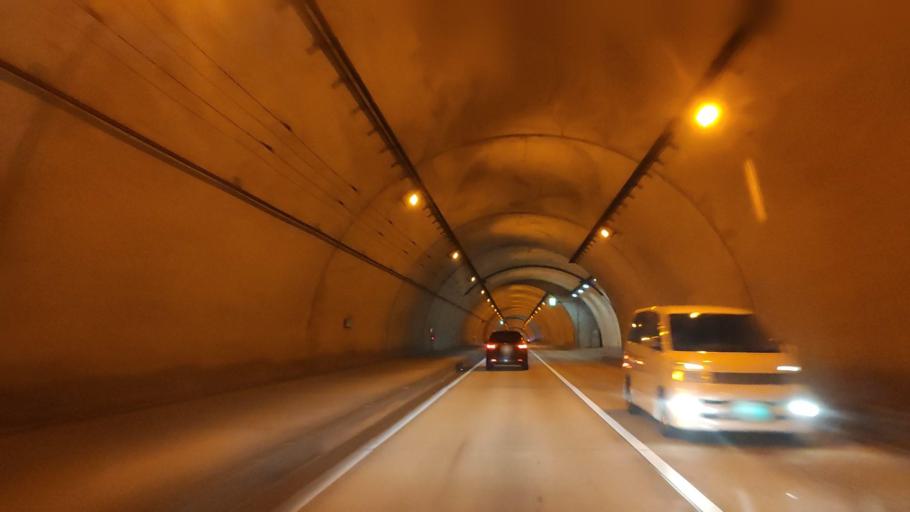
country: JP
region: Ehime
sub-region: Shikoku-chuo Shi
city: Matsuyama
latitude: 33.8803
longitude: 132.7115
